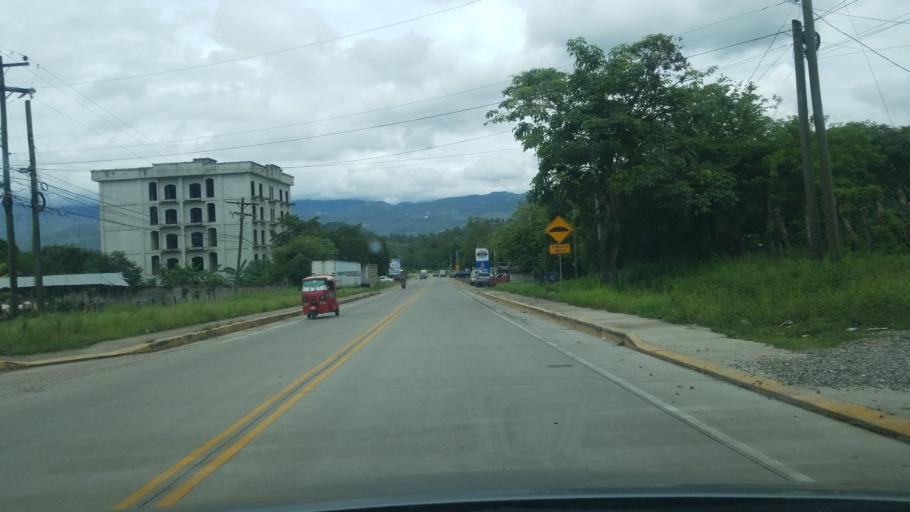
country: HN
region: Copan
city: La Entrada
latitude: 15.0679
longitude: -88.7616
